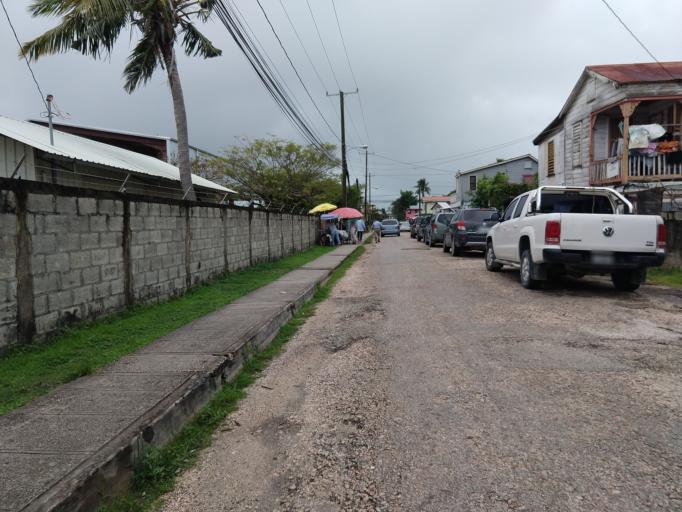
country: BZ
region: Belize
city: Belize City
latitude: 17.5038
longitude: -88.1915
